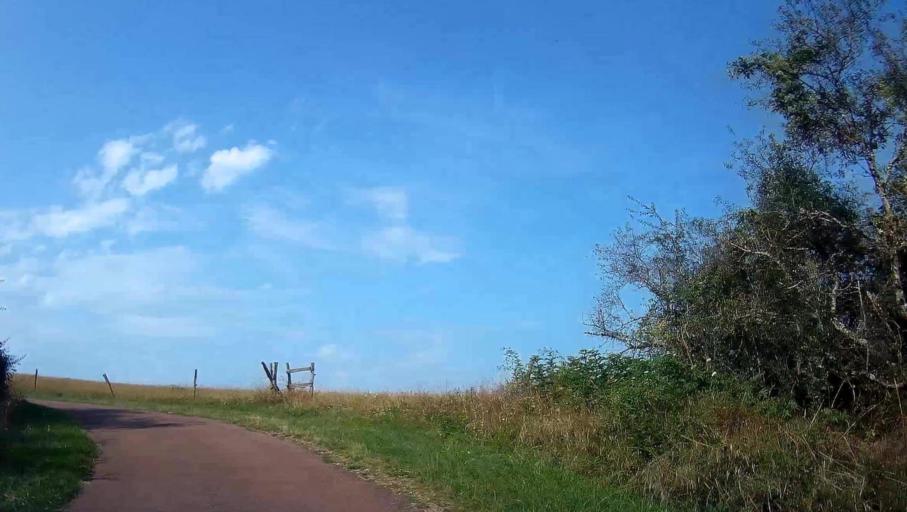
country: FR
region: Bourgogne
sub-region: Departement de la Cote-d'Or
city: Nolay
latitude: 46.9046
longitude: 4.6117
